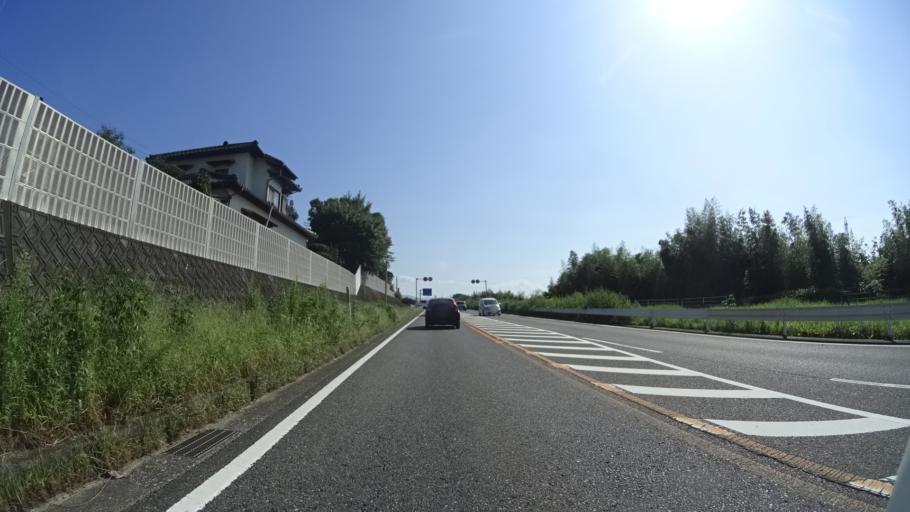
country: JP
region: Fukuoka
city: Yukuhashi
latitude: 33.6896
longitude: 130.9975
